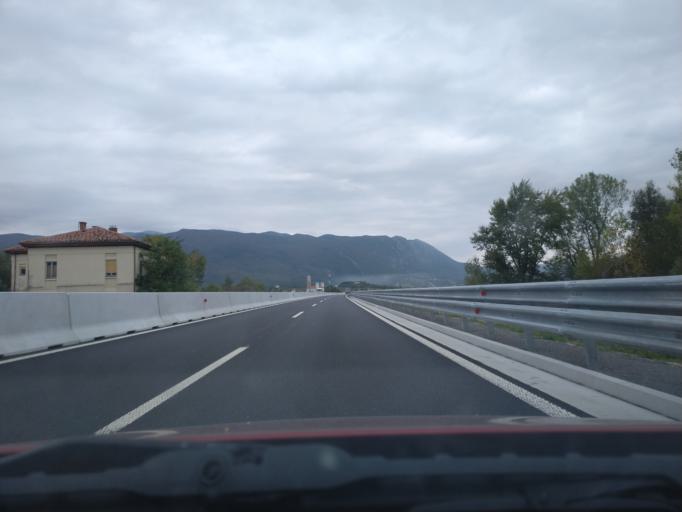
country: SI
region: Ajdovscina
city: Ajdovscina
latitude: 45.8709
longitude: 13.9265
